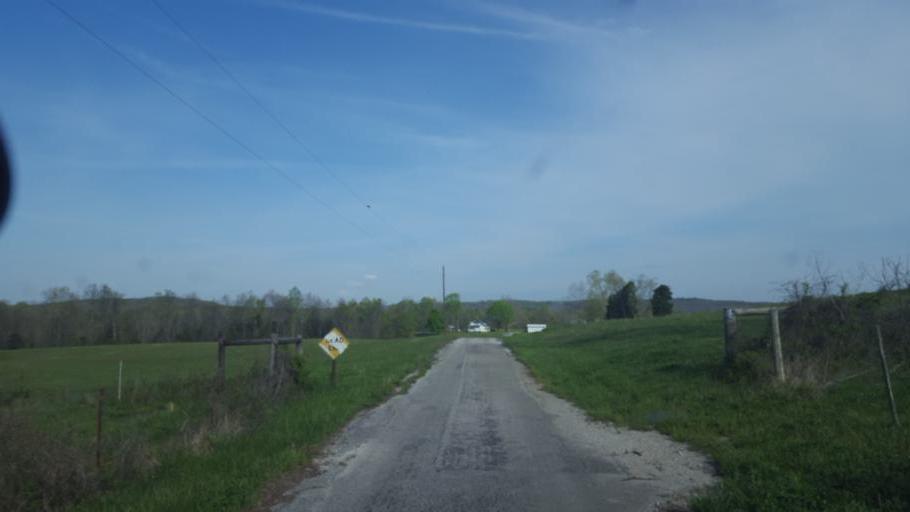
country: US
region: Kentucky
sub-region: Edmonson County
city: Brownsville
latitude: 37.3313
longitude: -86.1119
